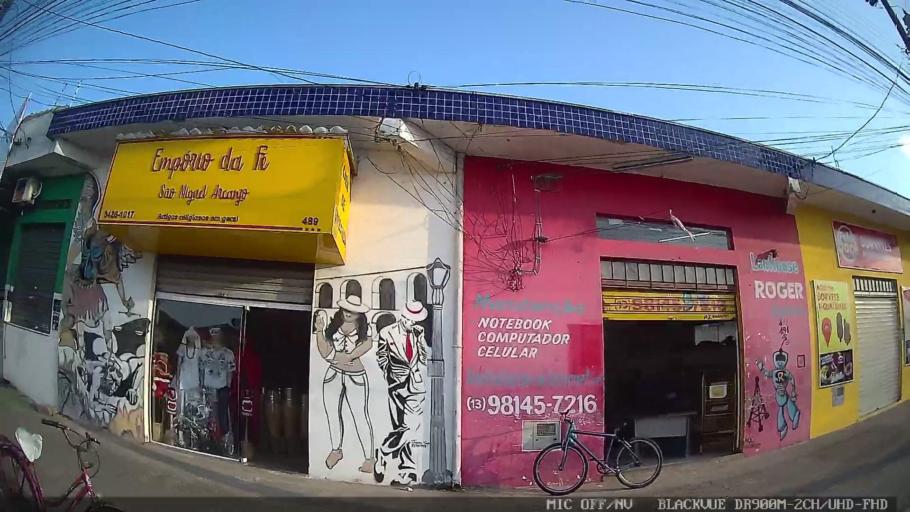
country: BR
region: Sao Paulo
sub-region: Itanhaem
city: Itanhaem
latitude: -24.1804
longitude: -46.8205
